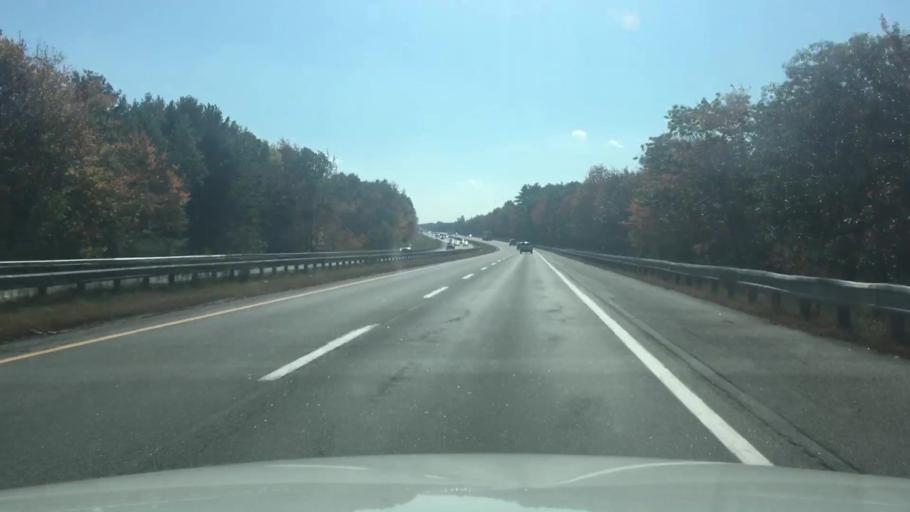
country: US
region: Maine
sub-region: Cumberland County
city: Westbrook
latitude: 43.6985
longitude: -70.3168
